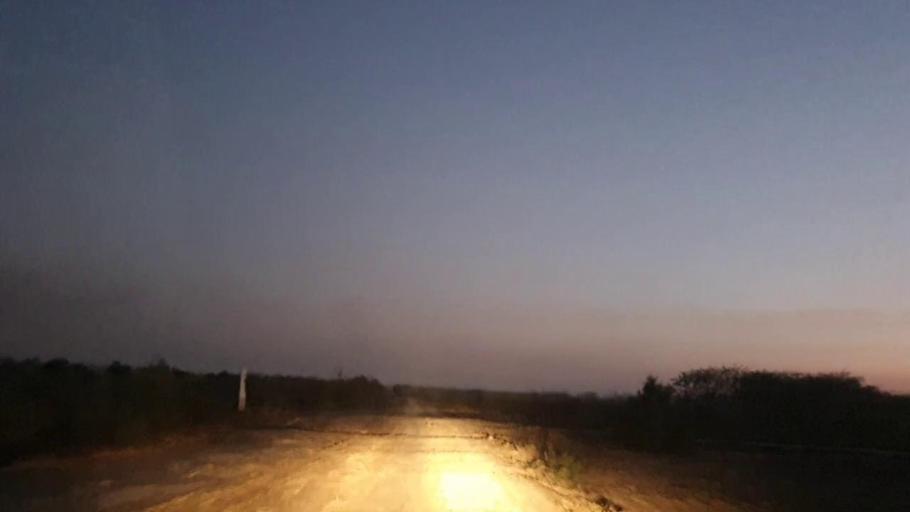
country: PK
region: Sindh
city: Nawabshah
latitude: 26.3243
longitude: 68.3779
